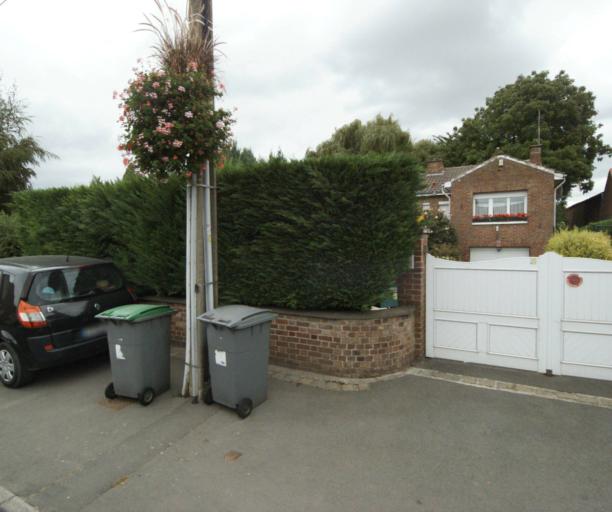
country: FR
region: Nord-Pas-de-Calais
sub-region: Departement du Nord
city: Fretin
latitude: 50.5564
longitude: 3.1377
